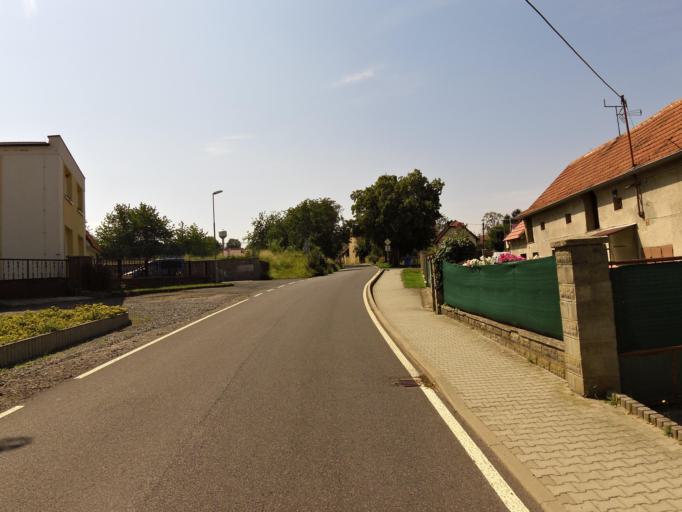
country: CZ
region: Central Bohemia
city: Cesky Brod
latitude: 50.0482
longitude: 14.8370
